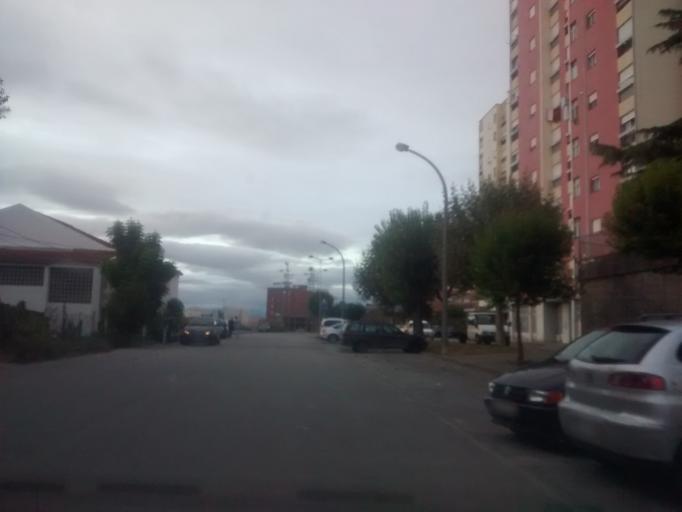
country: PT
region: Braga
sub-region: Braga
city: Braga
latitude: 41.5450
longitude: -8.4350
